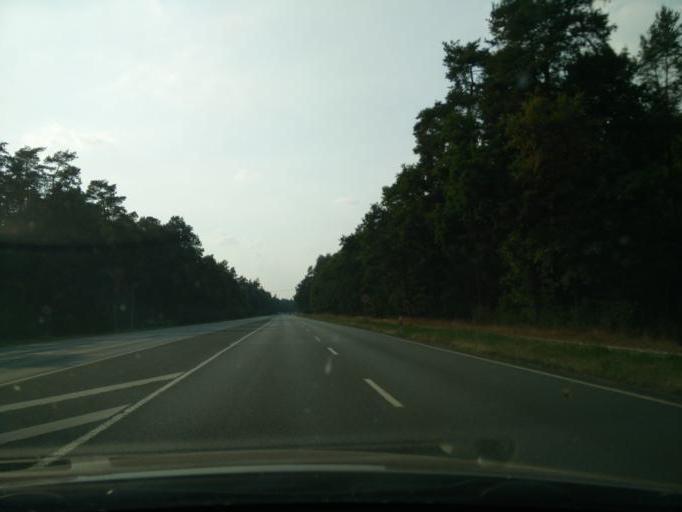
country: DE
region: Bavaria
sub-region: Regierungsbezirk Mittelfranken
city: Schwaig
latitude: 49.4214
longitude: 11.1587
